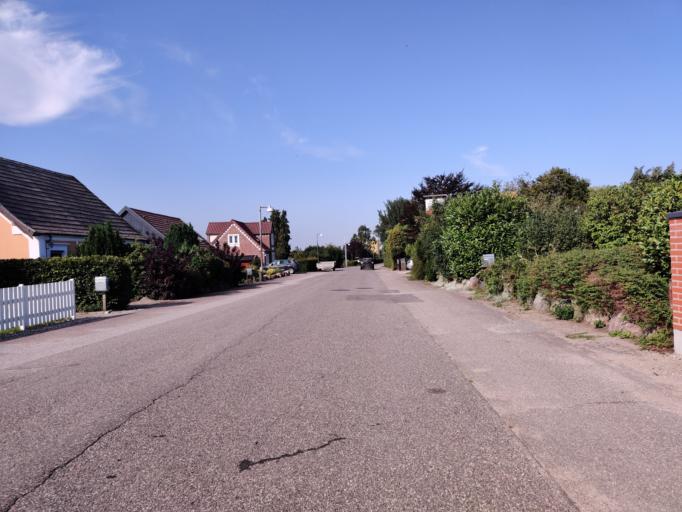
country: DK
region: Zealand
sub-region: Guldborgsund Kommune
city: Nykobing Falster
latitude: 54.7138
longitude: 11.9251
